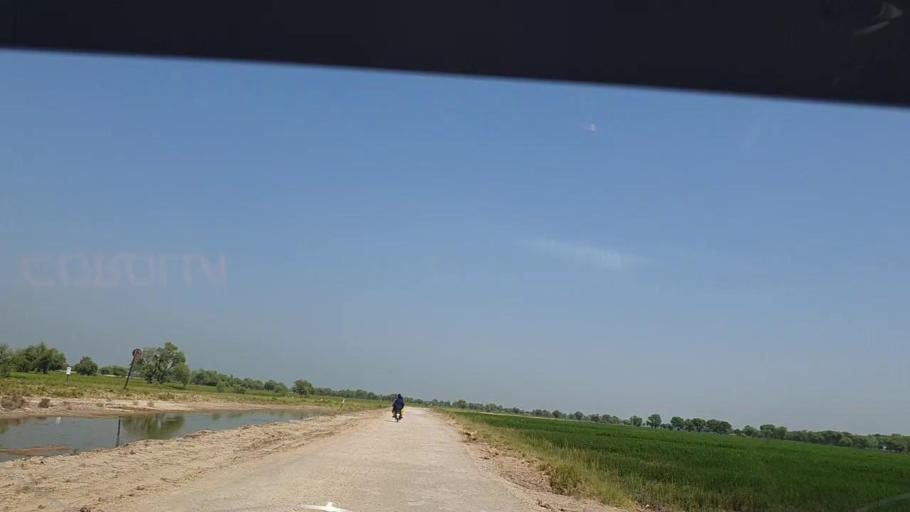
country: PK
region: Sindh
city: Tangwani
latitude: 28.2840
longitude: 69.0216
